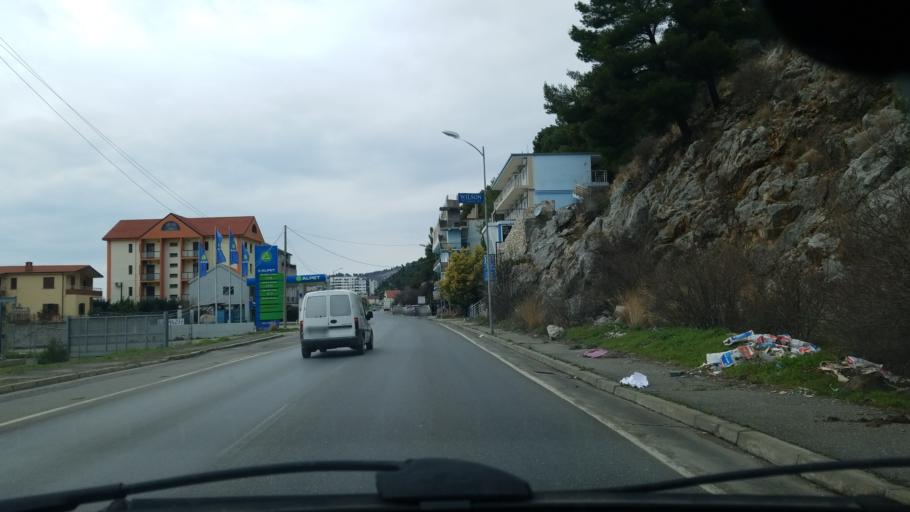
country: AL
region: Lezhe
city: Shengjin
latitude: 41.8062
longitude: 19.6098
